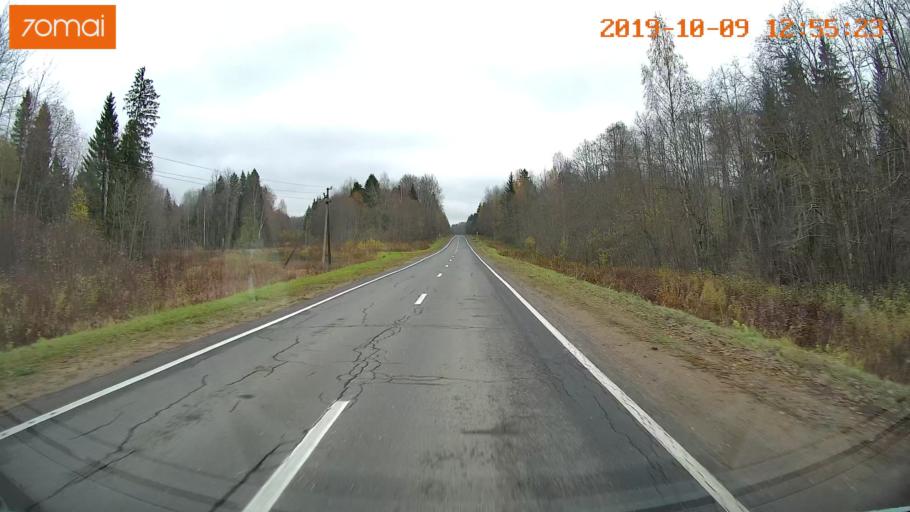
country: RU
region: Jaroslavl
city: Prechistoye
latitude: 58.4001
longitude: 40.3924
